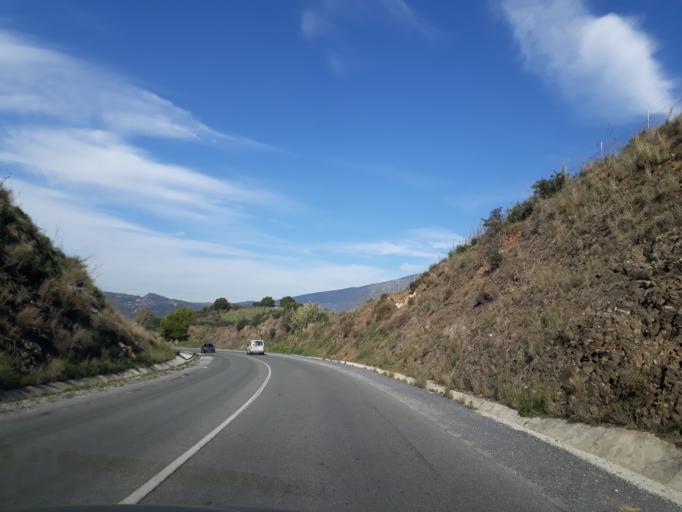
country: ES
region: Andalusia
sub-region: Provincia de Malaga
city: Fuengirola
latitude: 36.5356
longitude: -4.6859
